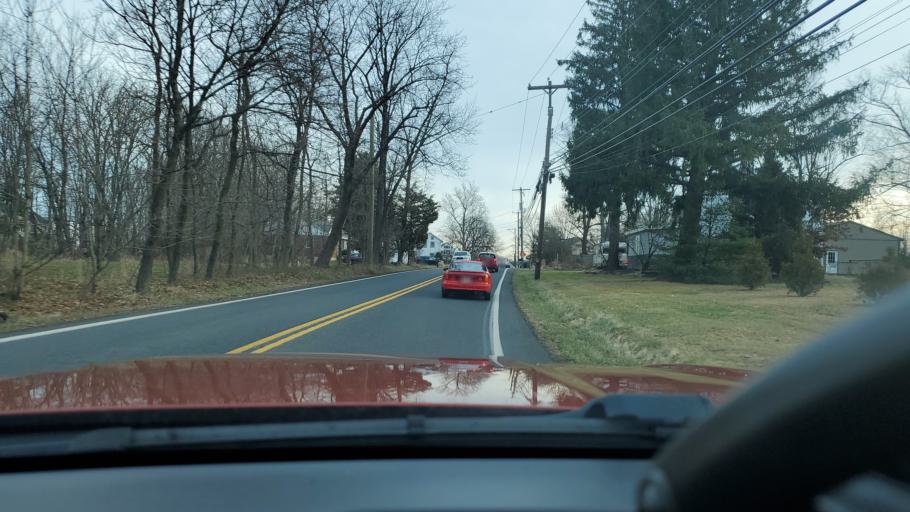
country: US
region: Pennsylvania
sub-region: Montgomery County
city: Woxall
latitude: 40.3462
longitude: -75.3949
